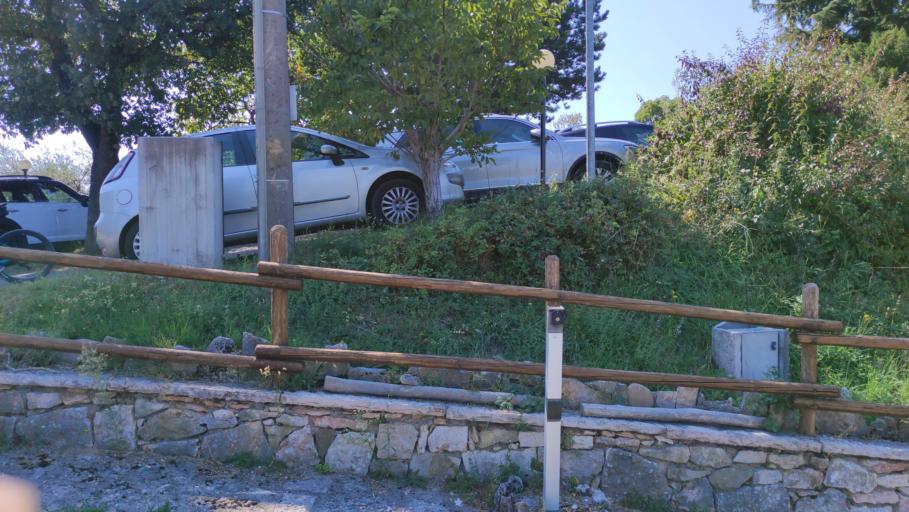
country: IT
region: Veneto
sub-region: Provincia di Verona
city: Costermano
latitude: 45.5713
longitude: 10.7396
